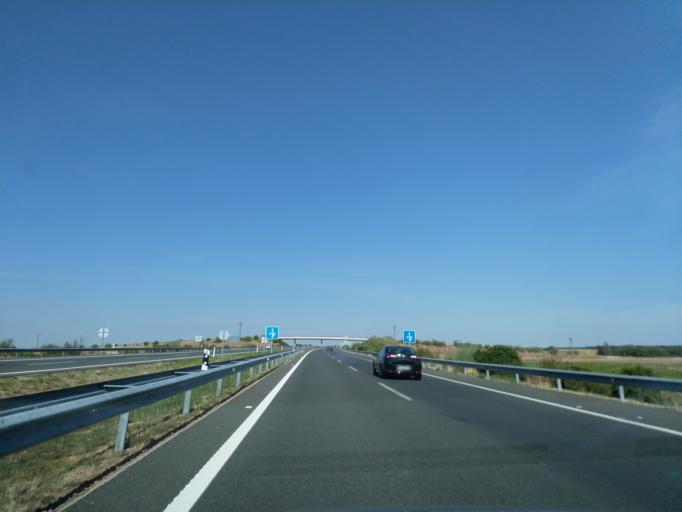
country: ES
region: Extremadura
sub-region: Provincia de Caceres
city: Aldea del Cano
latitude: 39.2814
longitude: -6.3267
